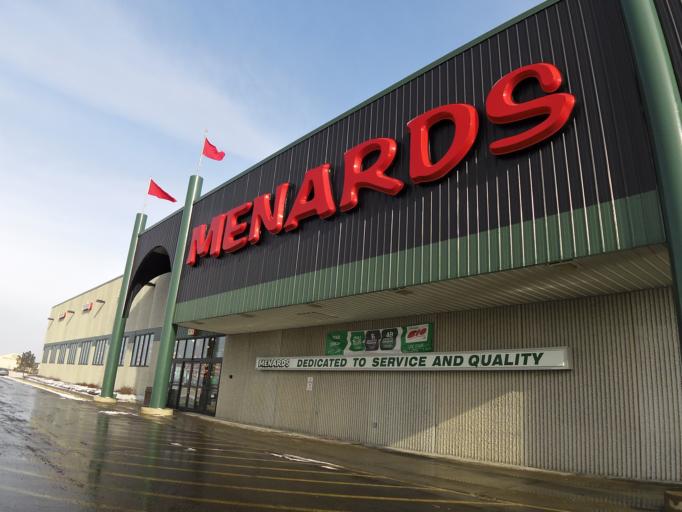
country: US
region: Minnesota
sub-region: McLeod County
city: Hutchinson
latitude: 44.8652
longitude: -94.3730
